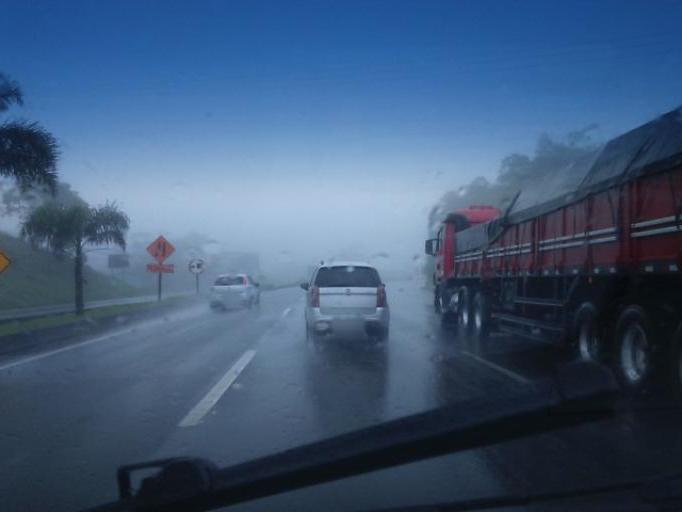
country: BR
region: Parana
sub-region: Guaratuba
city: Guaratuba
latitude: -25.8545
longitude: -48.9588
